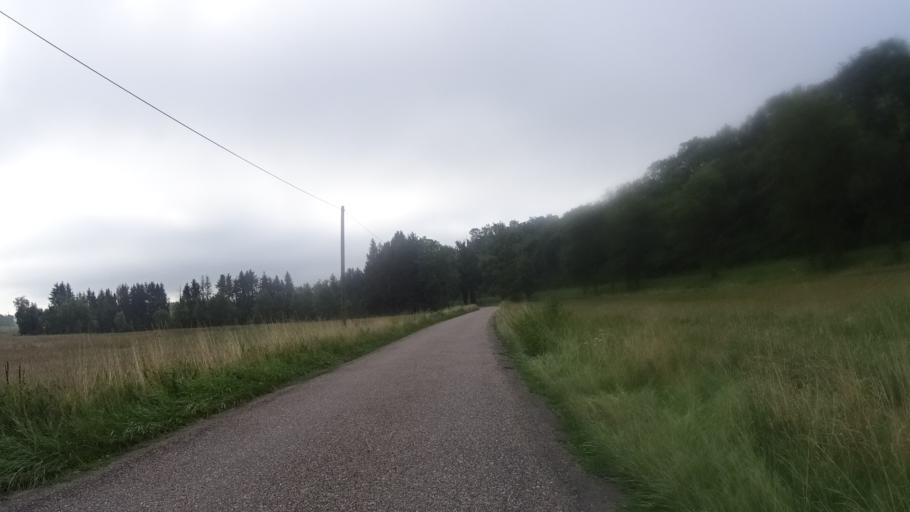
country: FR
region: Lorraine
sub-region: Departement de la Meuse
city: Revigny-sur-Ornain
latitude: 48.8049
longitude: 5.0556
